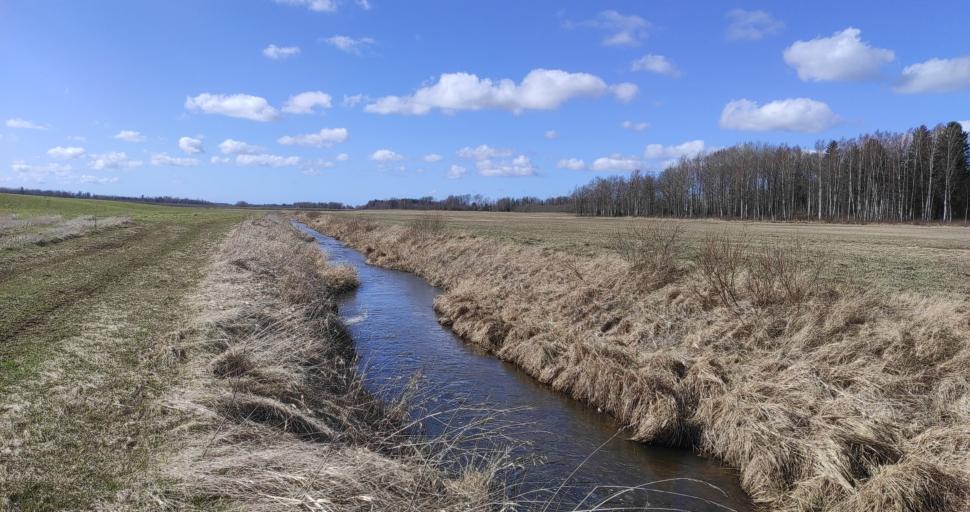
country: LV
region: Aizpute
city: Aizpute
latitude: 56.8462
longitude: 21.7497
